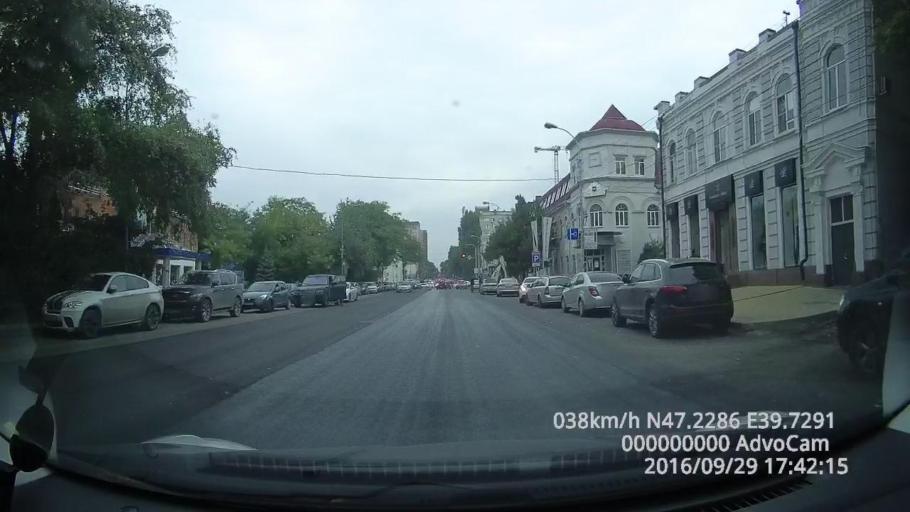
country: RU
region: Rostov
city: Rostov-na-Donu
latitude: 47.2287
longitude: 39.7290
